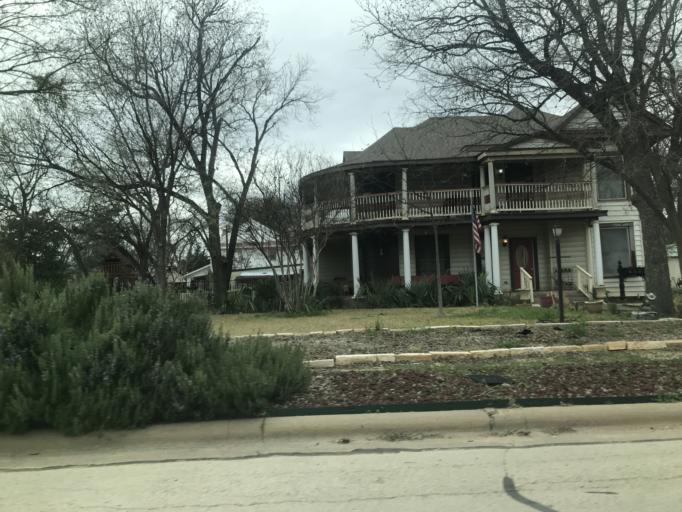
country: US
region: Texas
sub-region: Taylor County
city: Abilene
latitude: 32.4533
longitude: -99.7462
